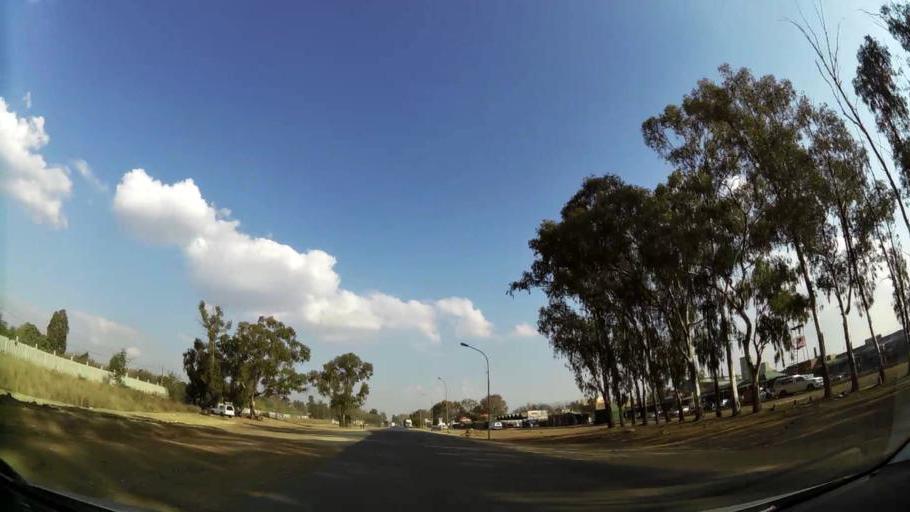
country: ZA
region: Gauteng
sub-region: Ekurhuleni Metropolitan Municipality
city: Tembisa
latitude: -25.9487
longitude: 28.2332
